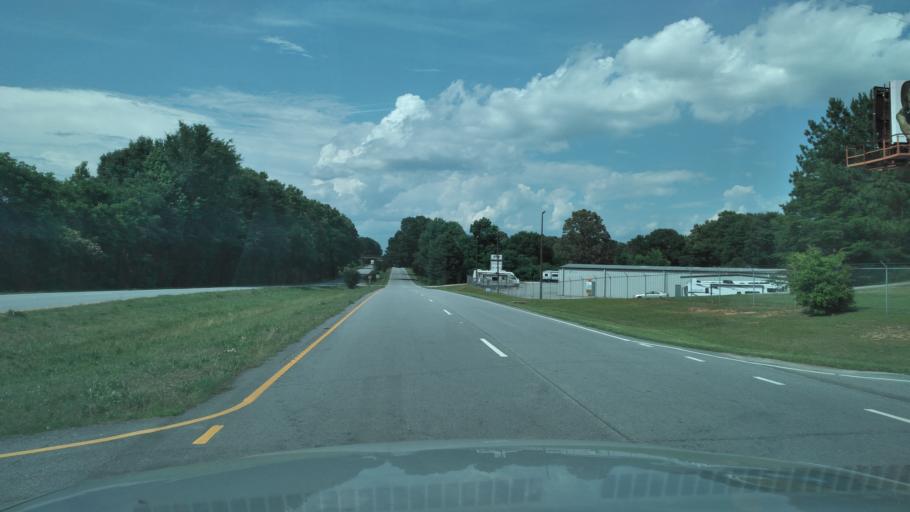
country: US
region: South Carolina
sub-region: Spartanburg County
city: Roebuck
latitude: 34.8629
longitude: -81.9616
